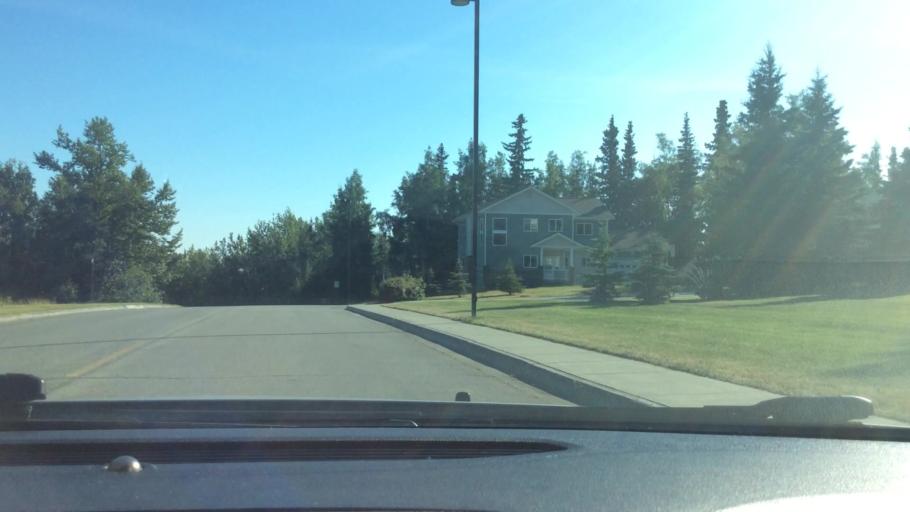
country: US
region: Alaska
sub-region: Anchorage Municipality
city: Elmendorf Air Force Base
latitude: 61.2507
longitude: -149.7009
